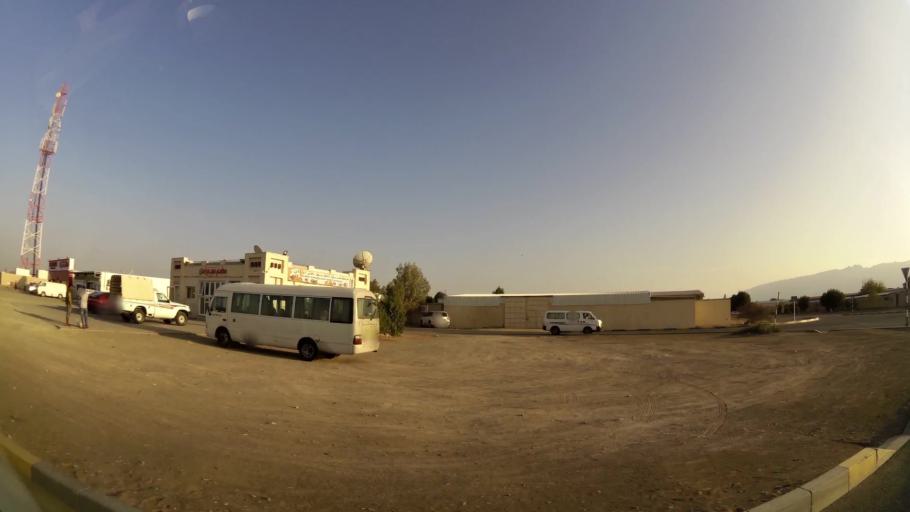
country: AE
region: Abu Dhabi
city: Al Ain
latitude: 24.1507
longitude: 55.8280
